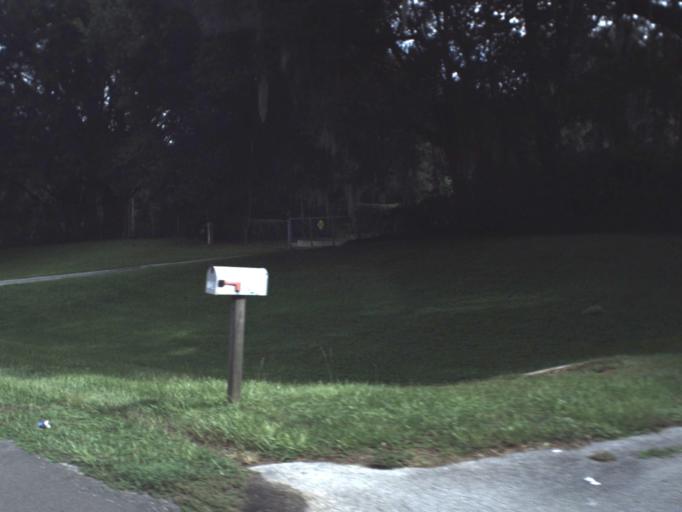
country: US
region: Florida
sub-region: Pasco County
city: Dade City
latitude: 28.3213
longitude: -82.1840
